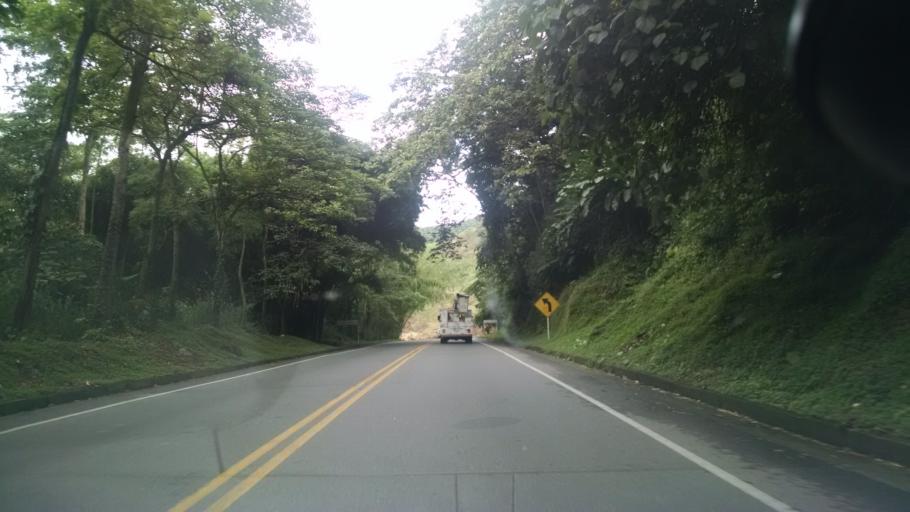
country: CO
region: Caldas
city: Palestina
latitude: 5.0612
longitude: -75.6105
